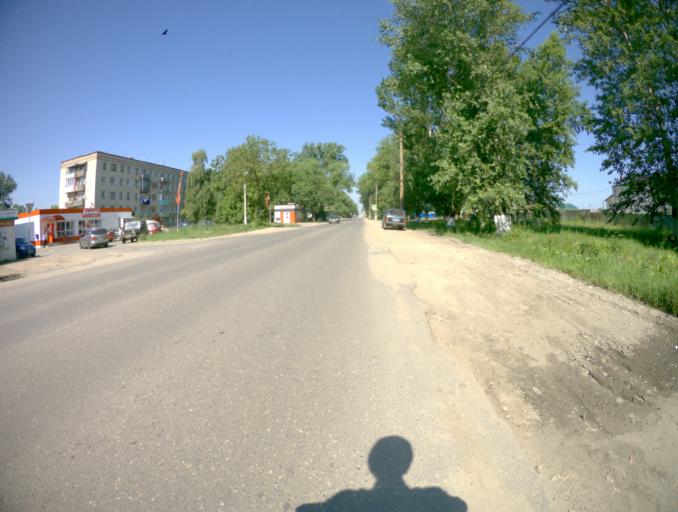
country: RU
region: Vladimir
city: Vyazniki
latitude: 56.2320
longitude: 42.1960
